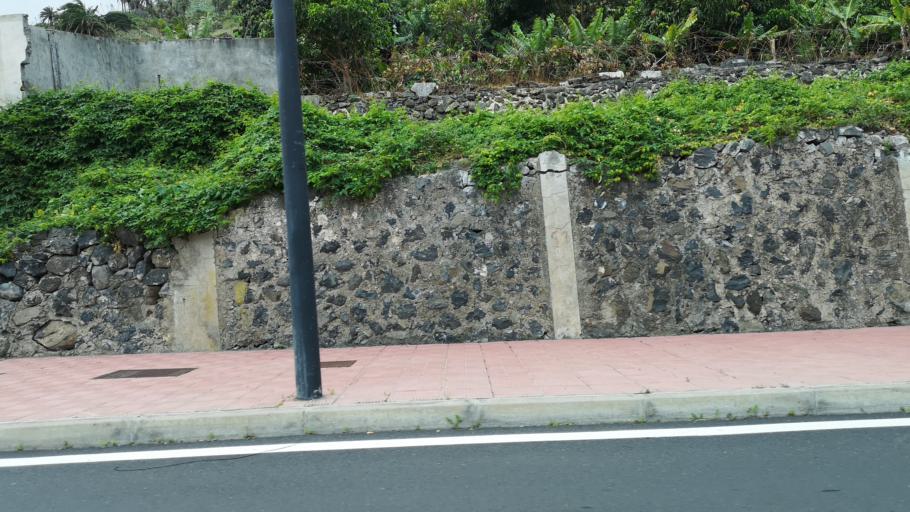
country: ES
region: Canary Islands
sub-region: Provincia de Santa Cruz de Tenerife
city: Hermigua
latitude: 28.1587
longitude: -17.1980
